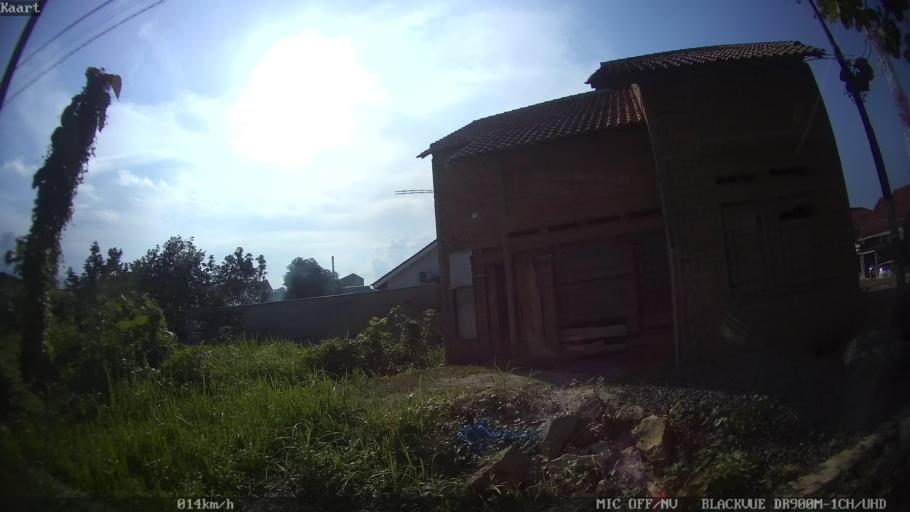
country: ID
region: Lampung
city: Kedaton
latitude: -5.3757
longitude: 105.2319
